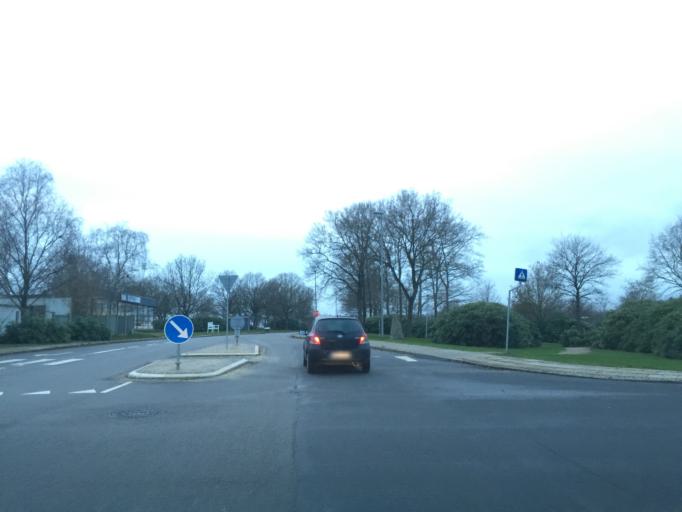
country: DK
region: Central Jutland
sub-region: Silkeborg Kommune
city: Kjellerup
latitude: 56.2834
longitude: 9.4330
